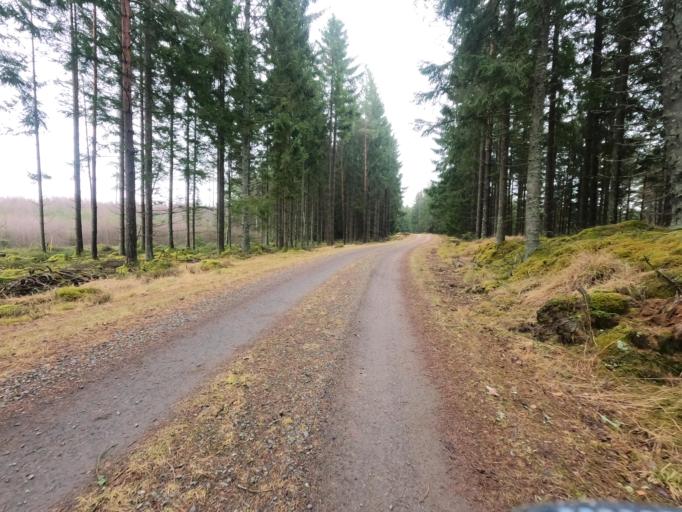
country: SE
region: Kronoberg
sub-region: Markaryds Kommun
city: Stromsnasbruk
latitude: 56.8091
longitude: 13.5688
